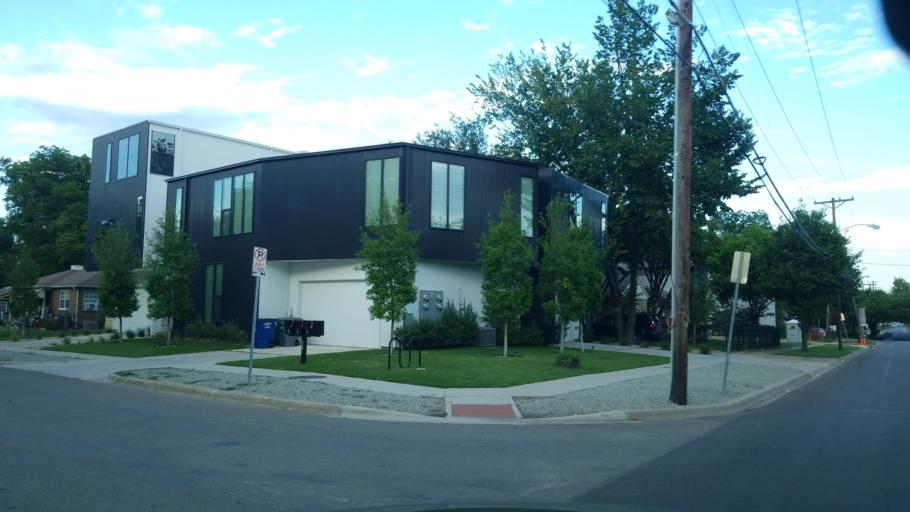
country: US
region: Texas
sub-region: Dallas County
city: Highland Park
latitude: 32.8087
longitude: -96.7871
